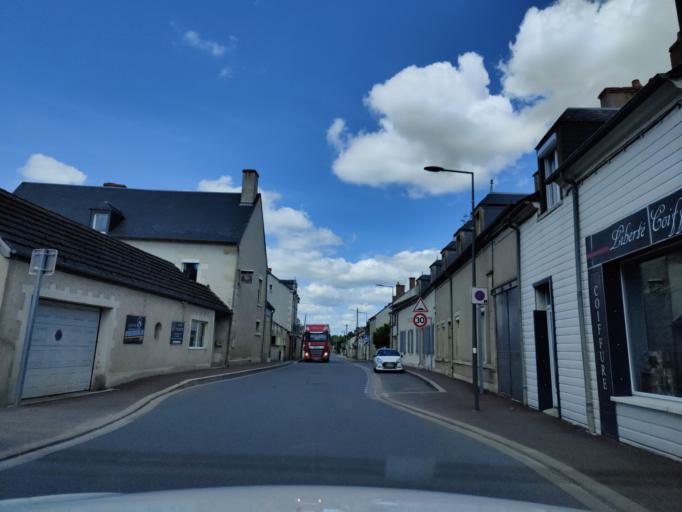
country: FR
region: Centre
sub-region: Departement du Cher
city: Levet
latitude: 46.9262
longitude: 2.4067
